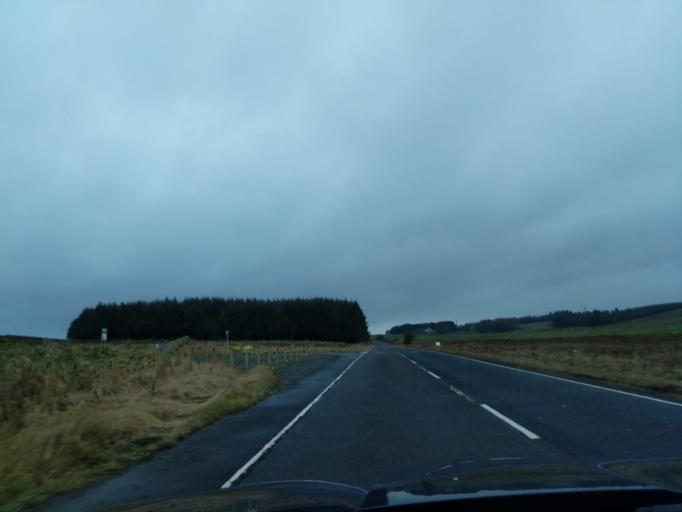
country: GB
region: England
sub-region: Northumberland
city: Corsenside
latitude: 55.1905
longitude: -2.0552
